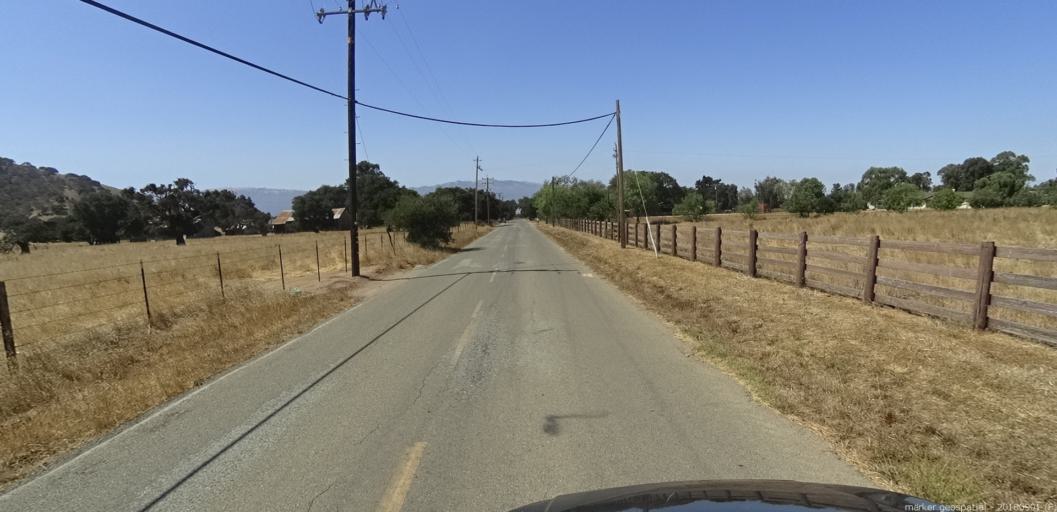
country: US
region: California
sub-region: Monterey County
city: Chualar
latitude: 36.5933
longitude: -121.4436
